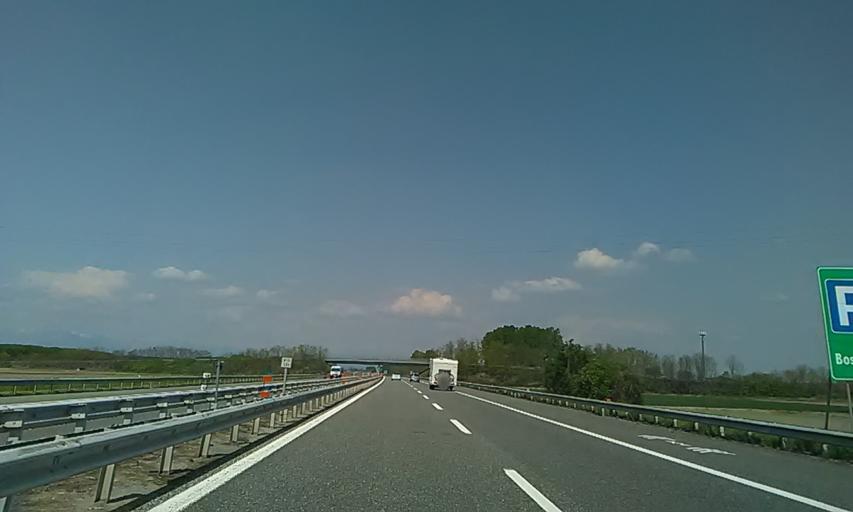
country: IT
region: Piedmont
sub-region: Provincia di Novara
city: Landiona
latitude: 45.4936
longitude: 8.4405
